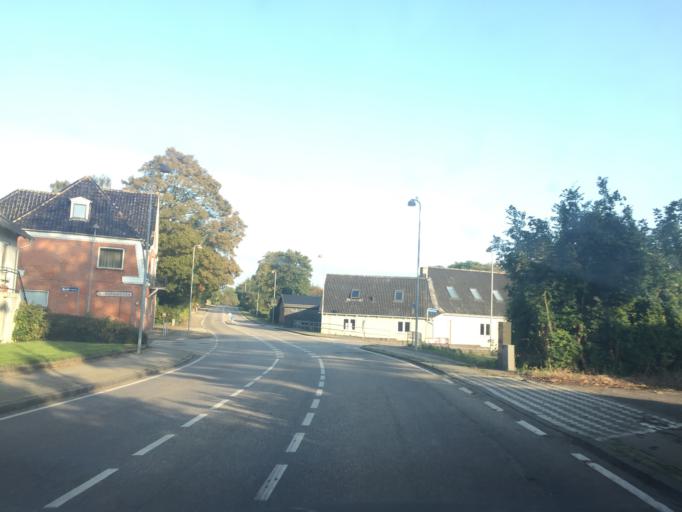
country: DK
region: Zealand
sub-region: Kalundborg Kommune
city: Svebolle
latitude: 55.6106
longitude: 11.2398
